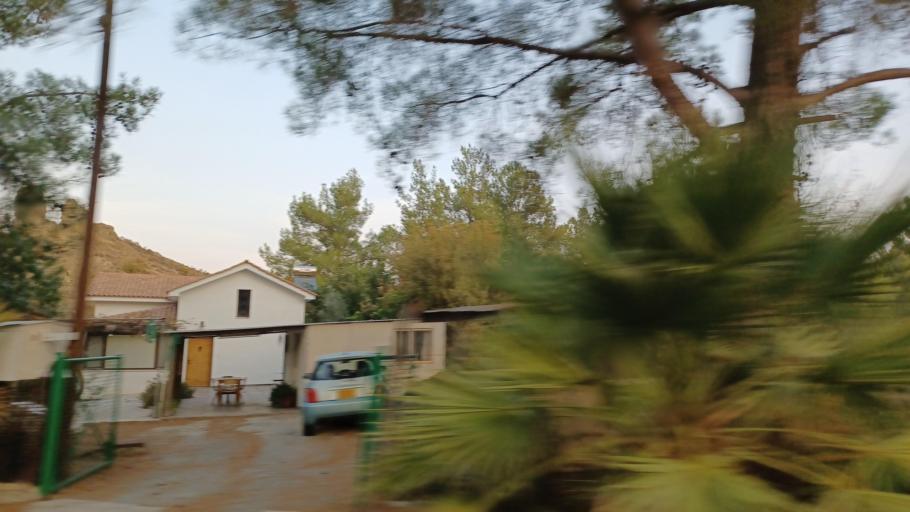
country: CY
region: Larnaka
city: Kornos
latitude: 34.9154
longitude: 33.3785
